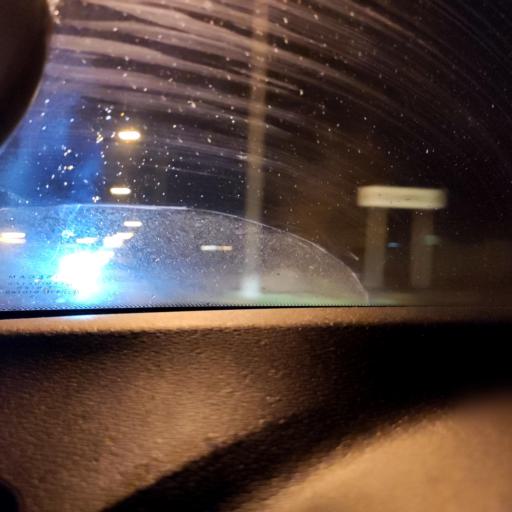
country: RU
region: Samara
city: Petra-Dubrava
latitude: 53.2720
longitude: 50.3844
